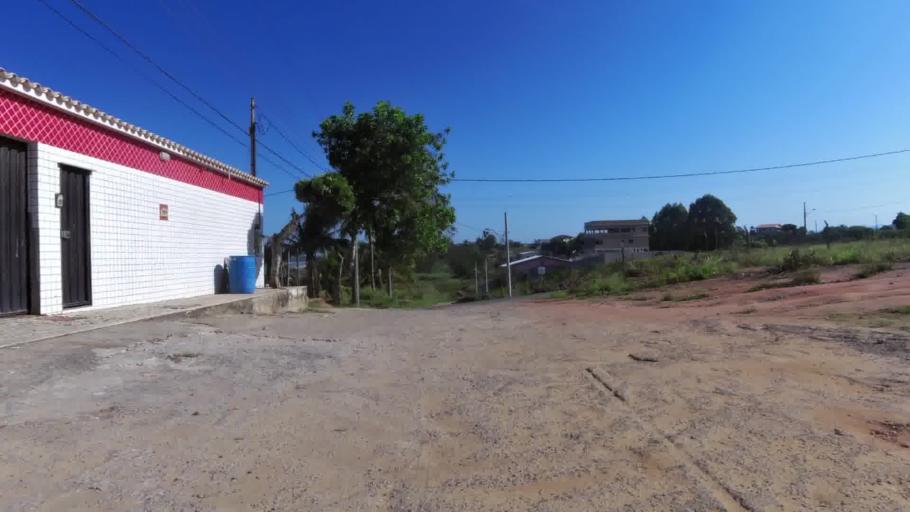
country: BR
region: Espirito Santo
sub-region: Guarapari
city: Guarapari
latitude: -20.7440
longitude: -40.5557
